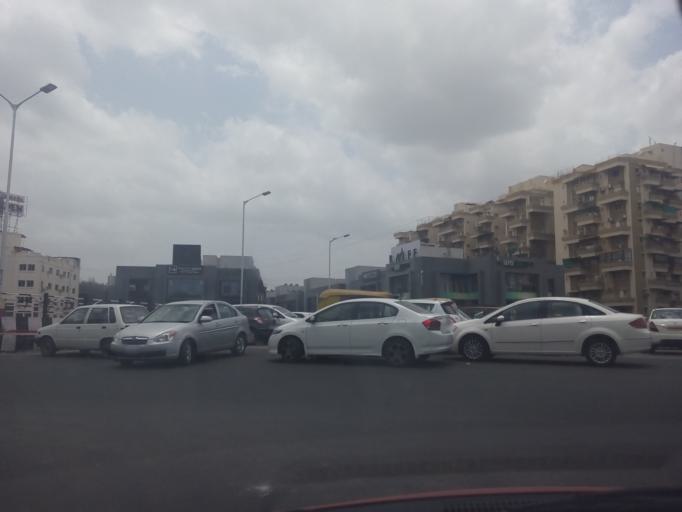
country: IN
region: Gujarat
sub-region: Ahmadabad
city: Sarkhej
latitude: 23.0462
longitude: 72.5159
